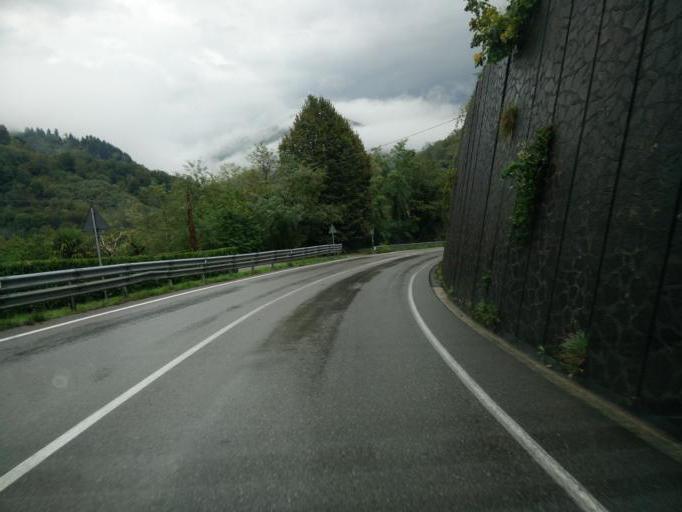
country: IT
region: Tuscany
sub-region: Provincia di Lucca
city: Fosciandora
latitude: 44.1161
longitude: 10.4362
